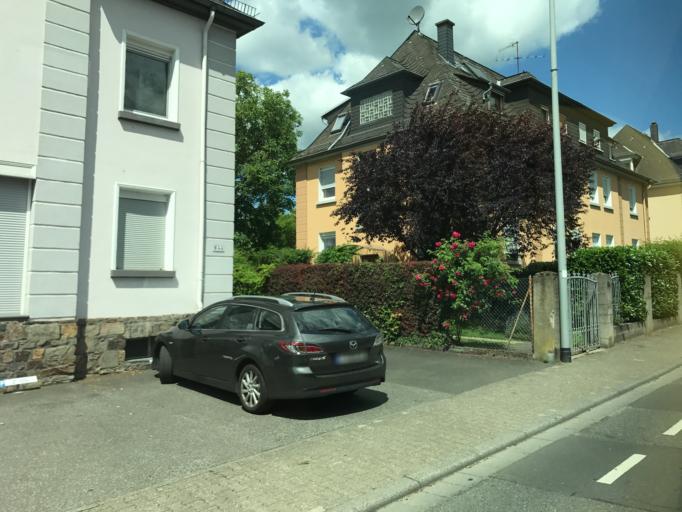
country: DE
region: Hesse
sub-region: Regierungsbezirk Darmstadt
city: Eltville
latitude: 50.0299
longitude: 8.1177
